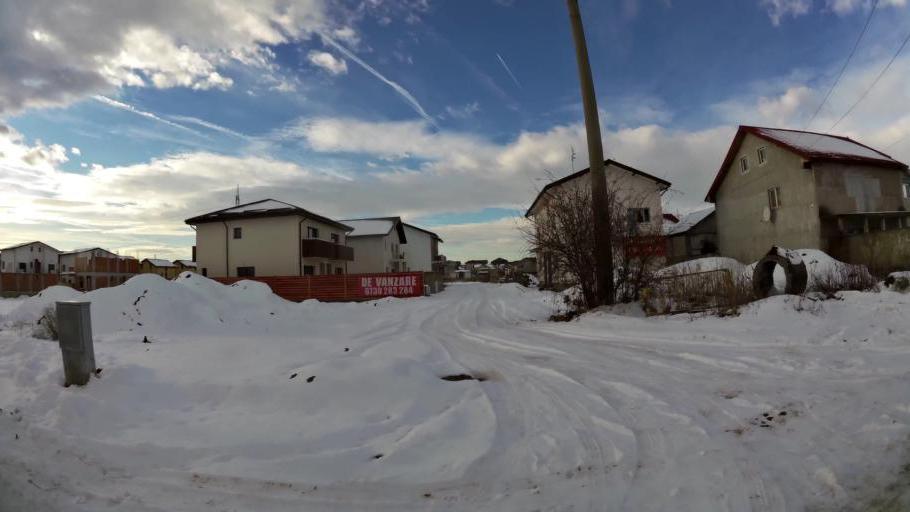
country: RO
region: Ilfov
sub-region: Comuna Fundeni-Dobroesti
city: Fundeni
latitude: 44.4652
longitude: 26.1773
